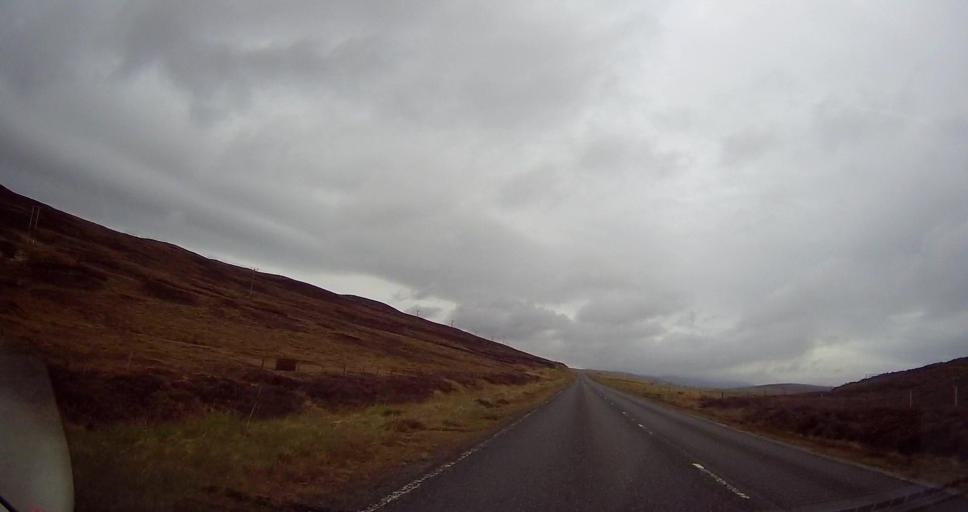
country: GB
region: Scotland
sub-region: Shetland Islands
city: Lerwick
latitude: 60.2118
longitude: -1.2338
